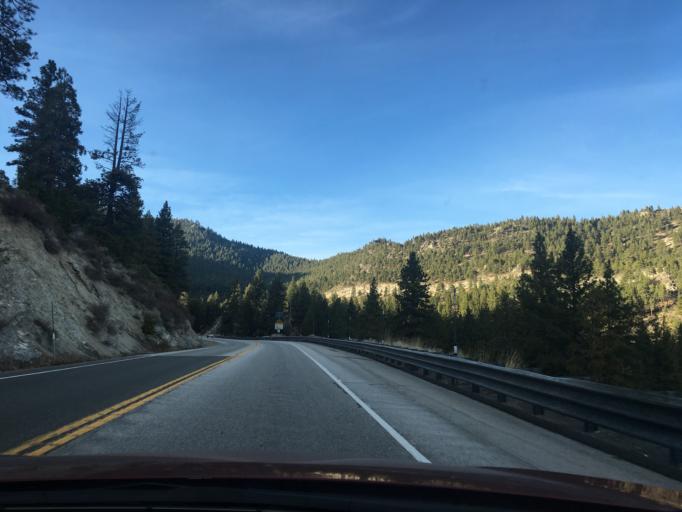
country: US
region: Nevada
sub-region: Douglas County
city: Kingsbury
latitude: 38.9730
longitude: -119.8566
